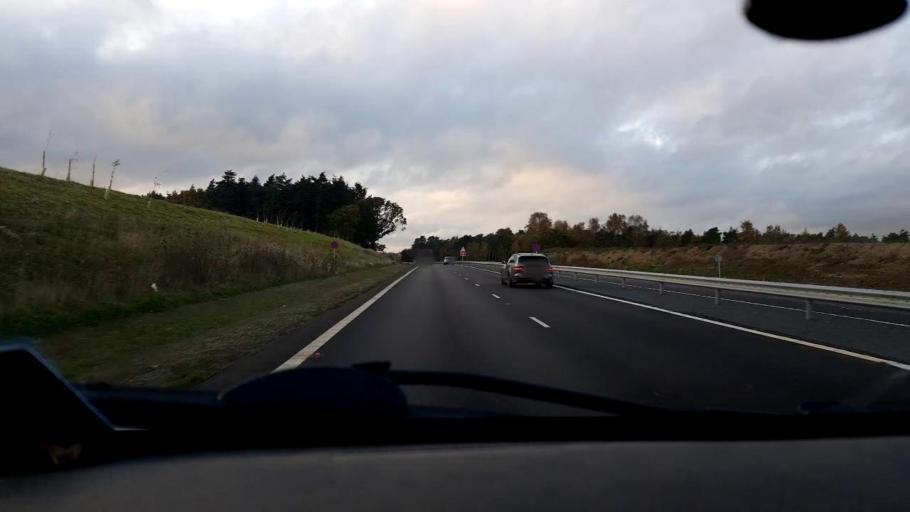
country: GB
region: England
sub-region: Norfolk
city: Horsford
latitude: 52.6947
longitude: 1.2204
